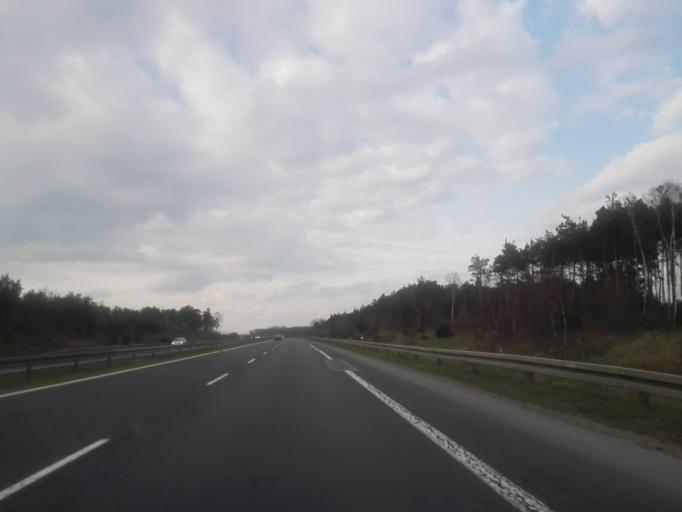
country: PL
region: Lodz Voivodeship
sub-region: Powiat radomszczanski
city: Kamiensk
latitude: 51.2443
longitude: 19.5231
